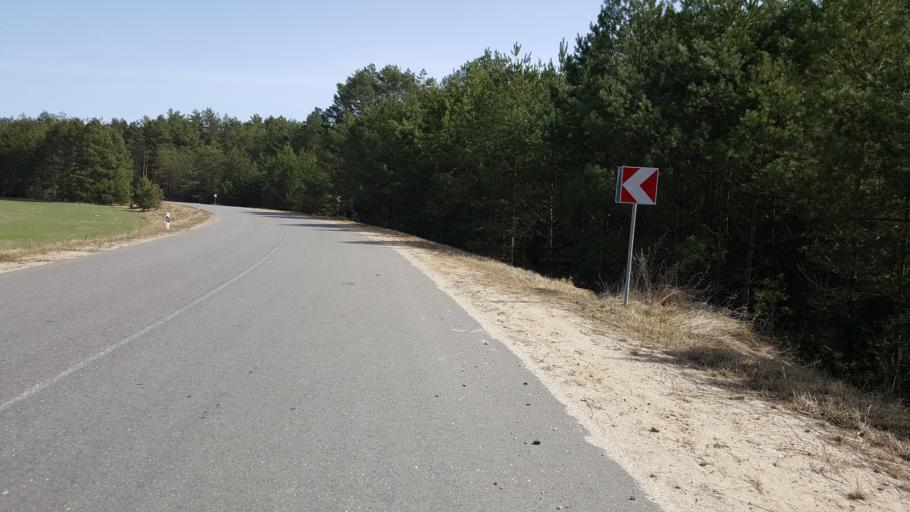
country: BY
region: Brest
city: Kamyanyuki
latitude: 52.5273
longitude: 23.8272
